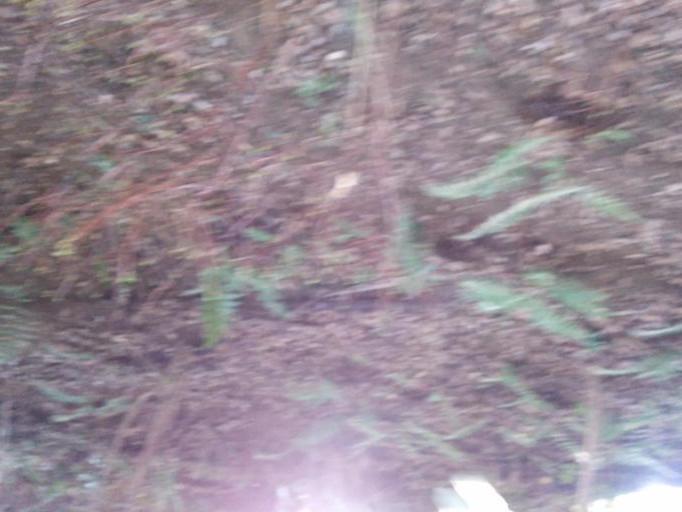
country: JP
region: Tokyo
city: Tokyo
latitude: 35.7045
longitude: 139.7498
